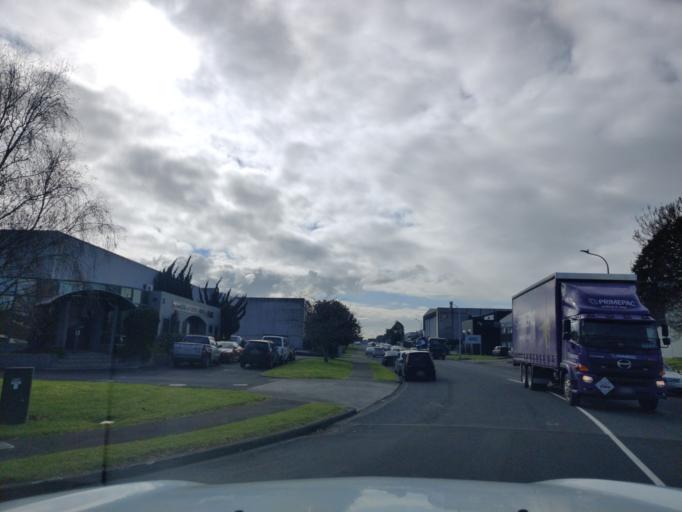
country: NZ
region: Auckland
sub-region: Auckland
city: Manukau City
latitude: -36.9414
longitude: 174.8813
